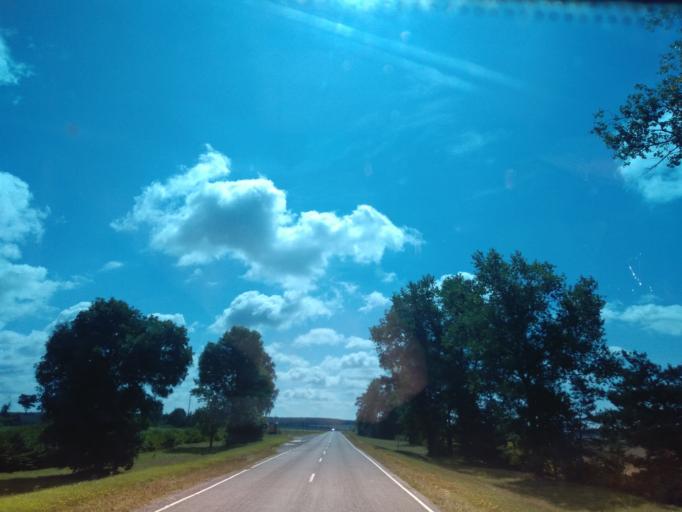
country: BY
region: Minsk
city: Uzda
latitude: 53.4022
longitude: 27.2263
